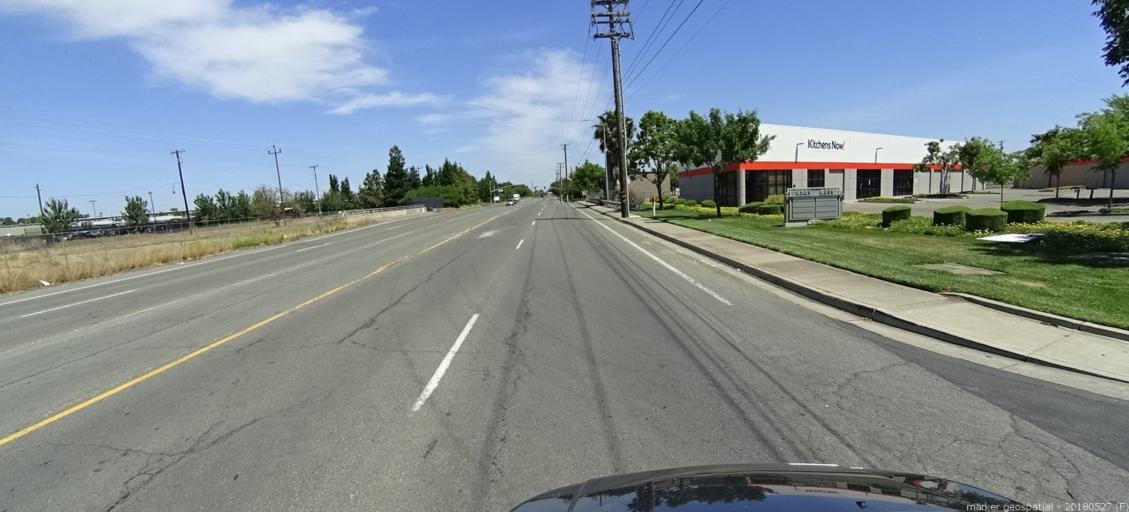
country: US
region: California
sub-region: Sacramento County
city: Florin
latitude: 38.5165
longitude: -121.3905
